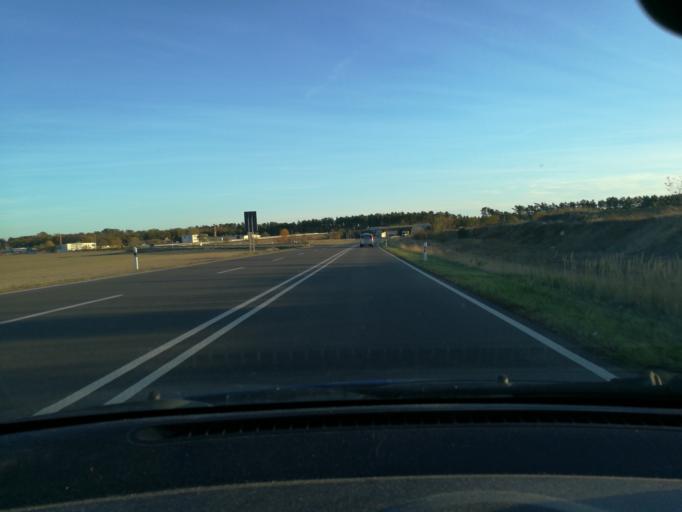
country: DE
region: Brandenburg
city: Perleberg
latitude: 53.0651
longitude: 11.8312
